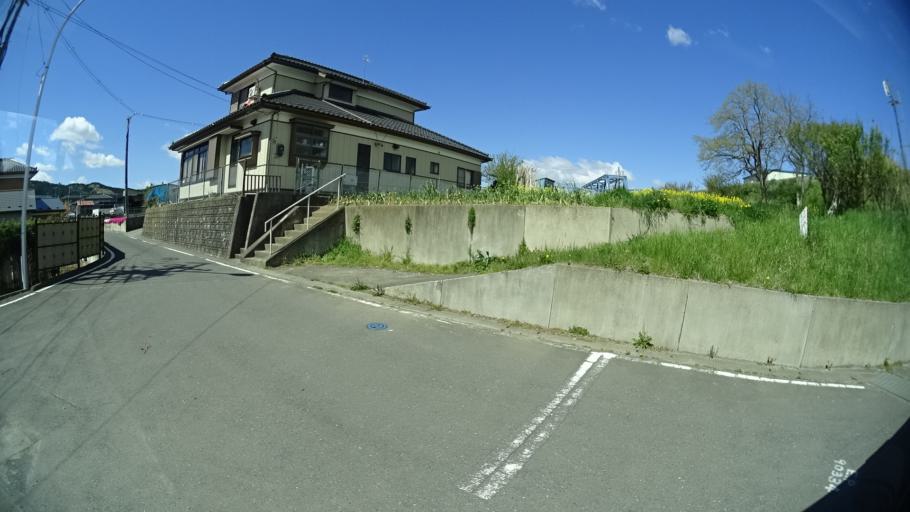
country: JP
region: Miyagi
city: Wakuya
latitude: 38.6086
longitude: 141.3010
